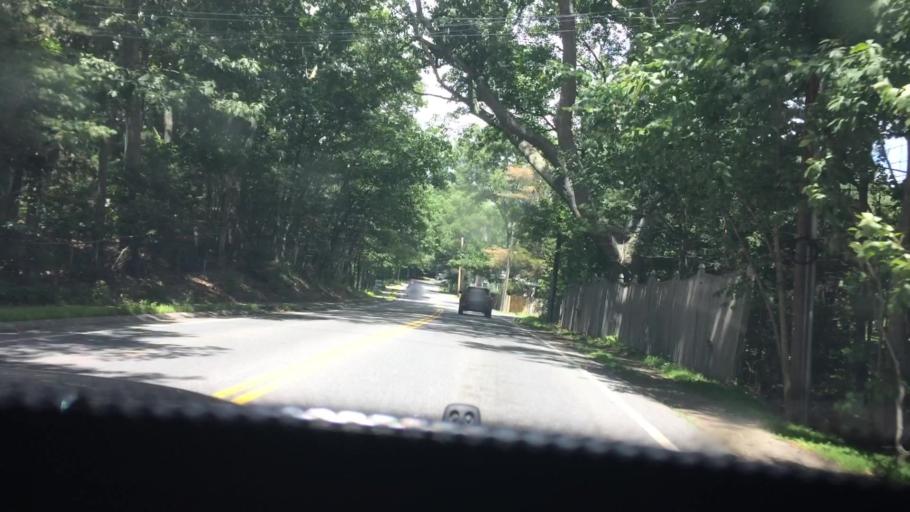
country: US
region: Massachusetts
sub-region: Middlesex County
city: Sudbury
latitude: 42.3919
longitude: -71.4224
